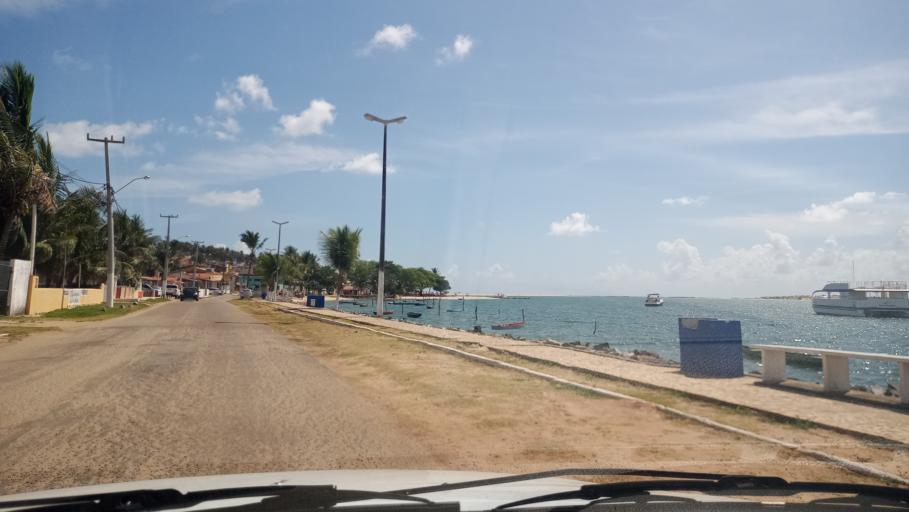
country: BR
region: Rio Grande do Norte
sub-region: Canguaretama
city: Canguaretama
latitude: -6.3168
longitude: -35.0450
